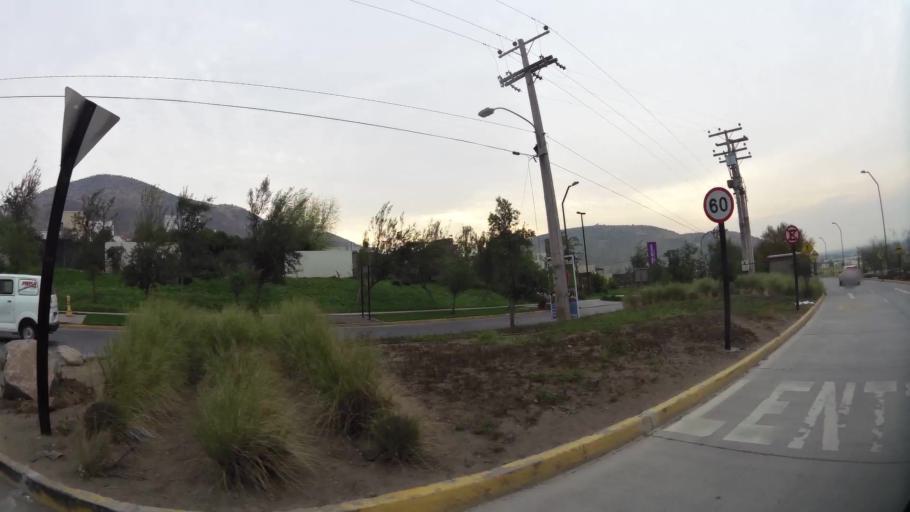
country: CL
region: Santiago Metropolitan
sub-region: Provincia de Chacabuco
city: Chicureo Abajo
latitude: -33.3202
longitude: -70.6495
